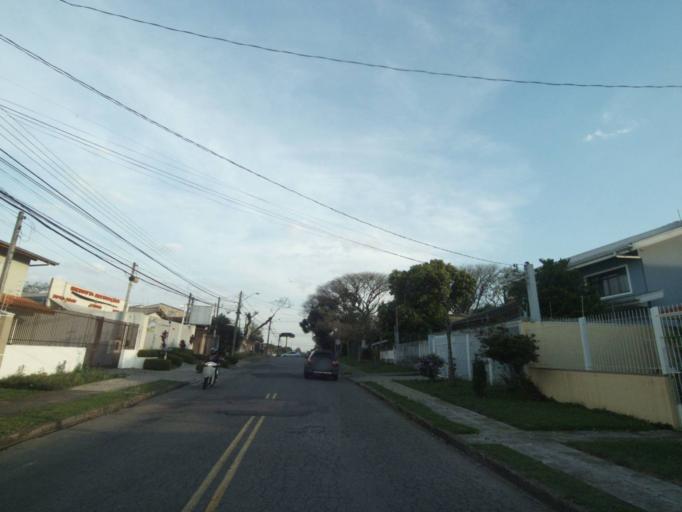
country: BR
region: Parana
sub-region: Curitiba
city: Curitiba
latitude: -25.4580
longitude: -49.3096
